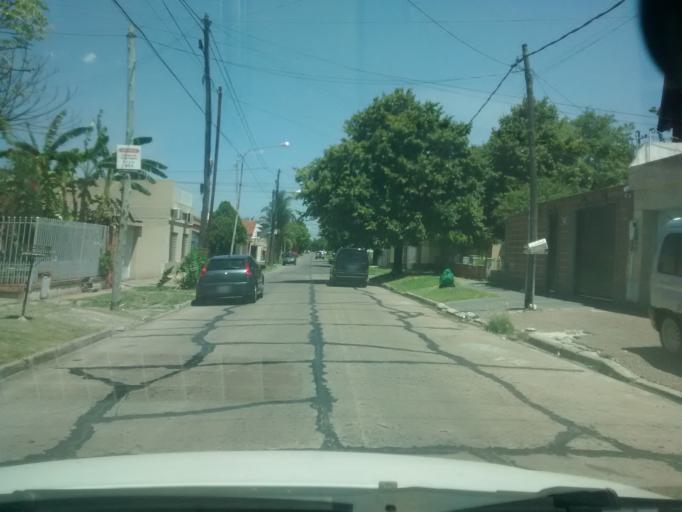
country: AR
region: Buenos Aires
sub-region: Partido de Moron
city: Moron
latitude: -34.6628
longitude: -58.6069
